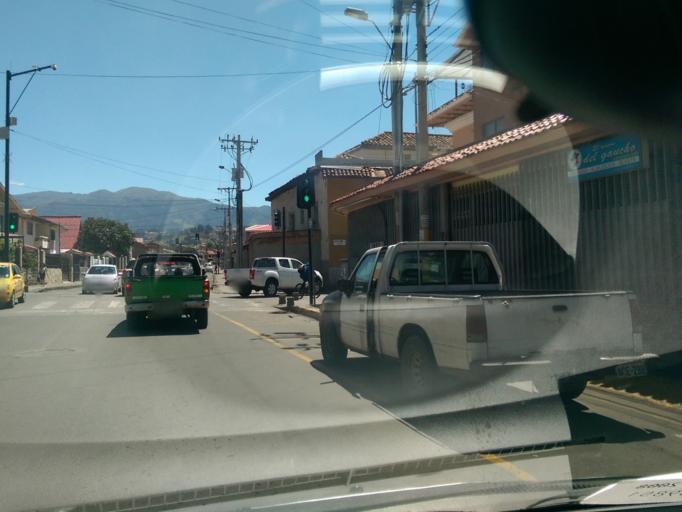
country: EC
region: Azuay
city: Cuenca
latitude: -2.9031
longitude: -79.0200
